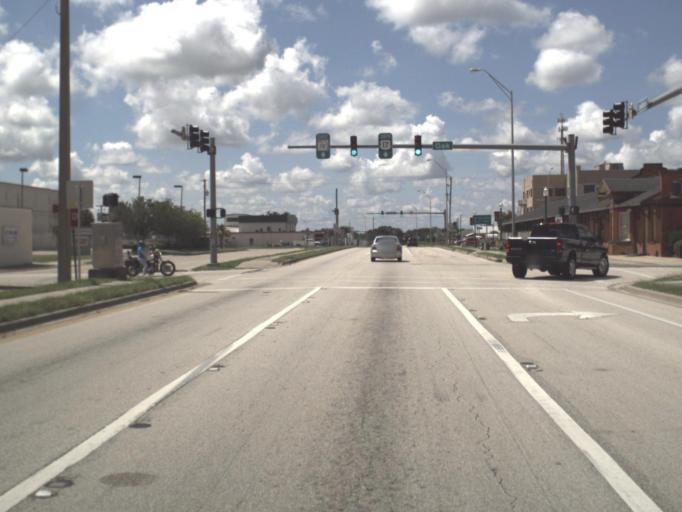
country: US
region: Florida
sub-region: DeSoto County
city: Arcadia
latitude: 27.2157
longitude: -81.8600
